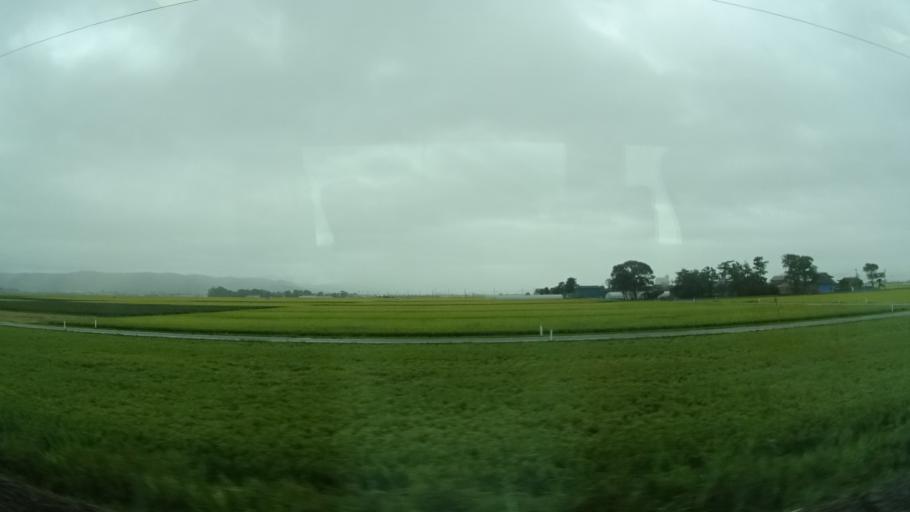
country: JP
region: Yamagata
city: Sakata
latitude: 38.8165
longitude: 139.9089
